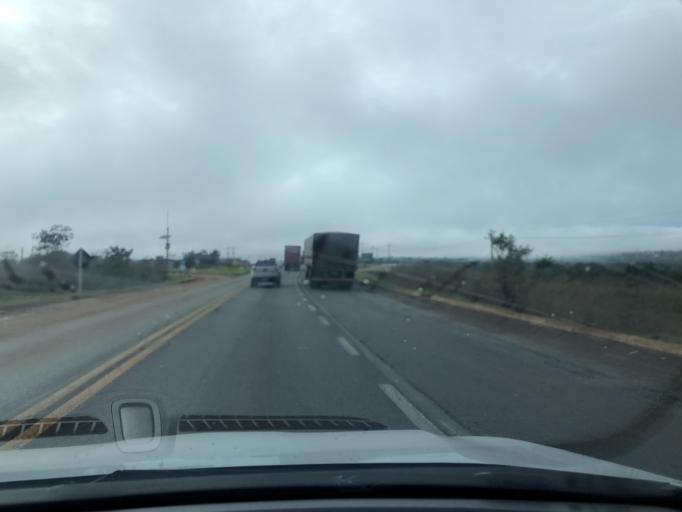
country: BR
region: Goias
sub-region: Cristalina
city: Cristalina
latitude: -16.7332
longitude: -47.6224
